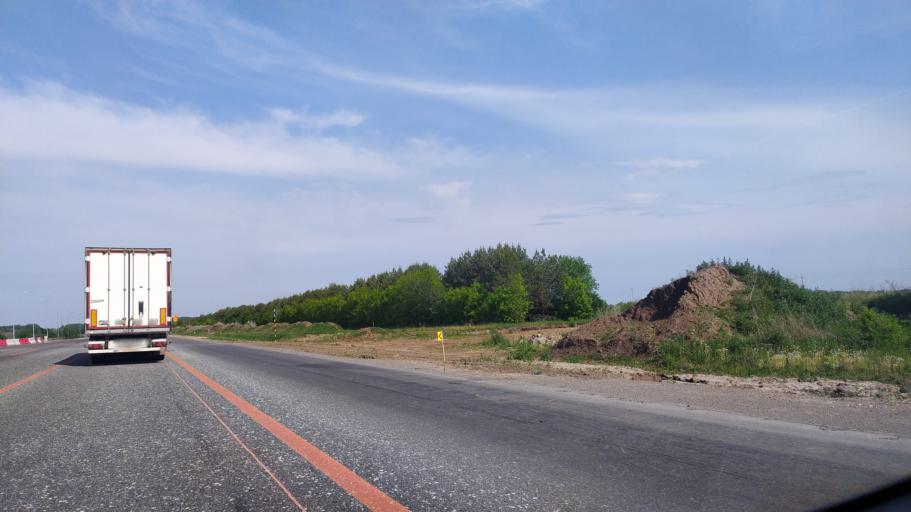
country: RU
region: Mariy-El
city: Volzhsk
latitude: 55.7267
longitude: 48.3769
